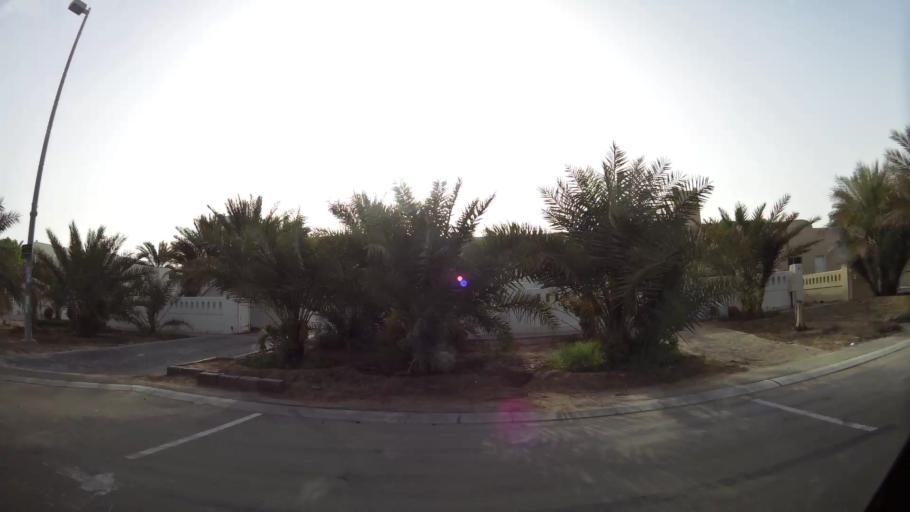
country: AE
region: Abu Dhabi
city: Al Ain
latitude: 24.1178
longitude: 55.7115
